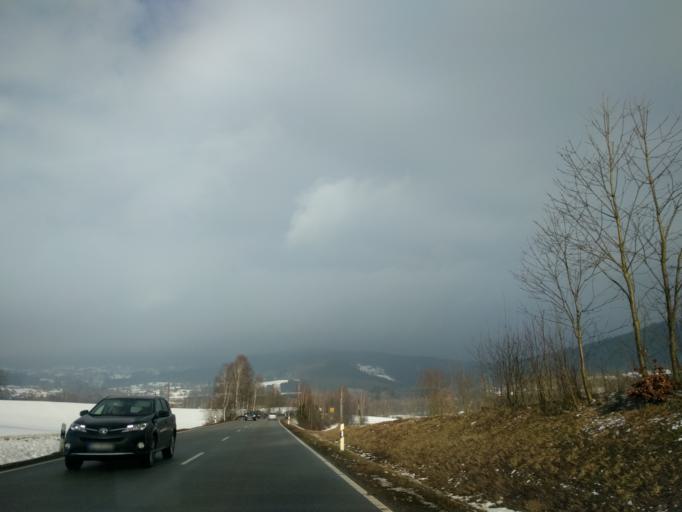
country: DE
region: Bavaria
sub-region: Lower Bavaria
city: Zwiesel
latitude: 49.0289
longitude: 13.2400
